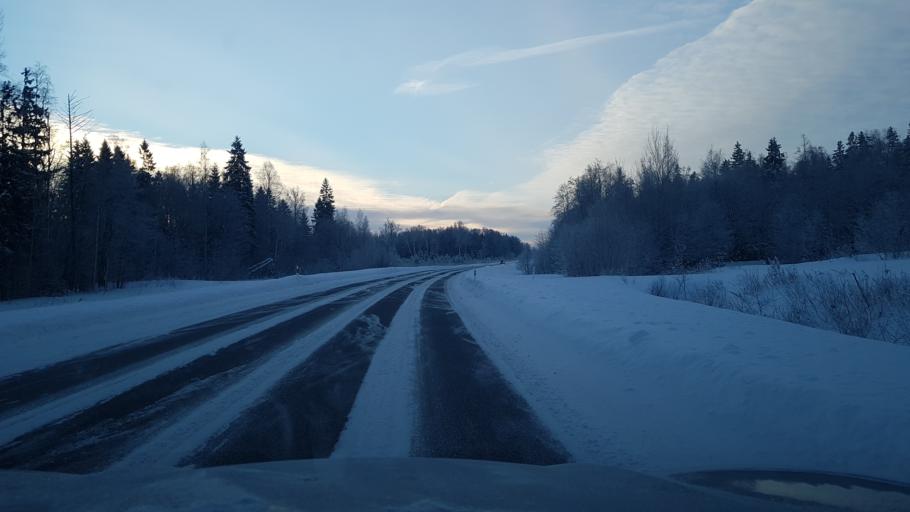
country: EE
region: Ida-Virumaa
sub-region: Johvi vald
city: Johvi
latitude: 59.3529
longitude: 27.4671
